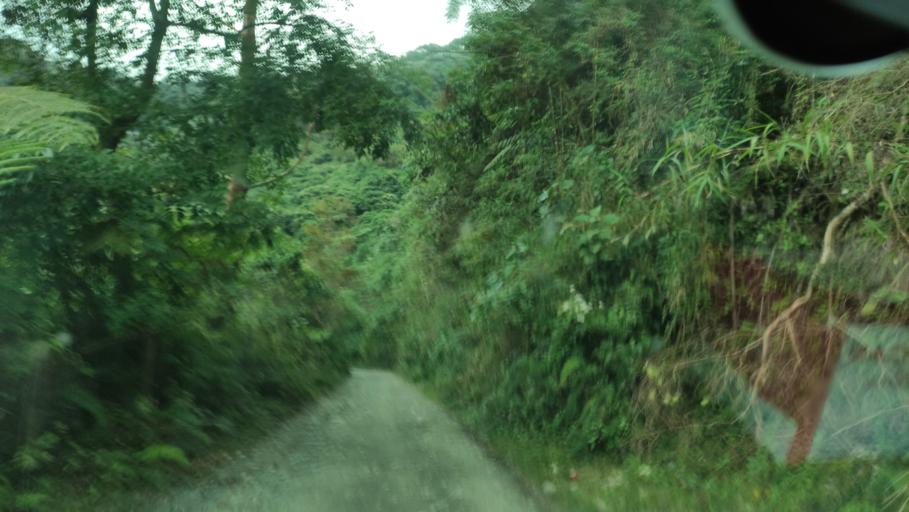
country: CO
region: Valle del Cauca
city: San Pedro
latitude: 3.8797
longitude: -76.1502
